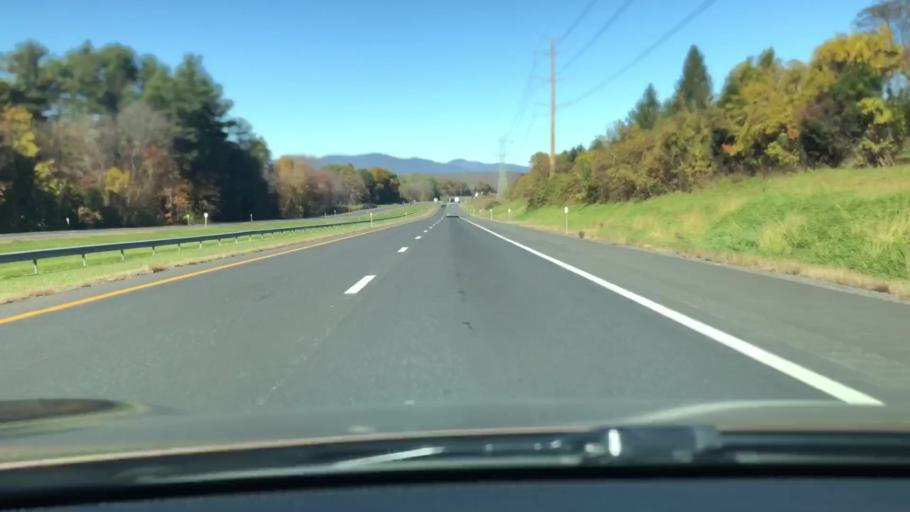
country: US
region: New York
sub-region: Ulster County
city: Hurley
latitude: 41.9124
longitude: -74.0432
